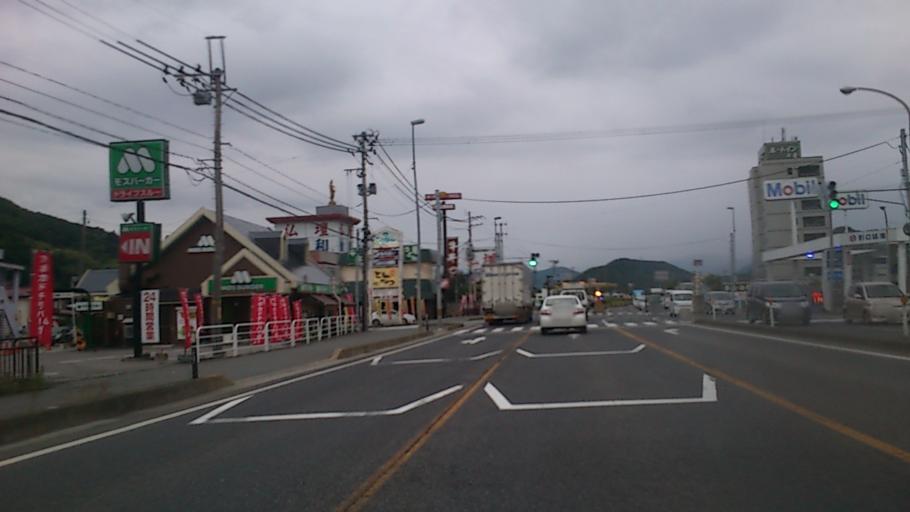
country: JP
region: Yamagata
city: Tendo
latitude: 38.3614
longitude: 140.3882
